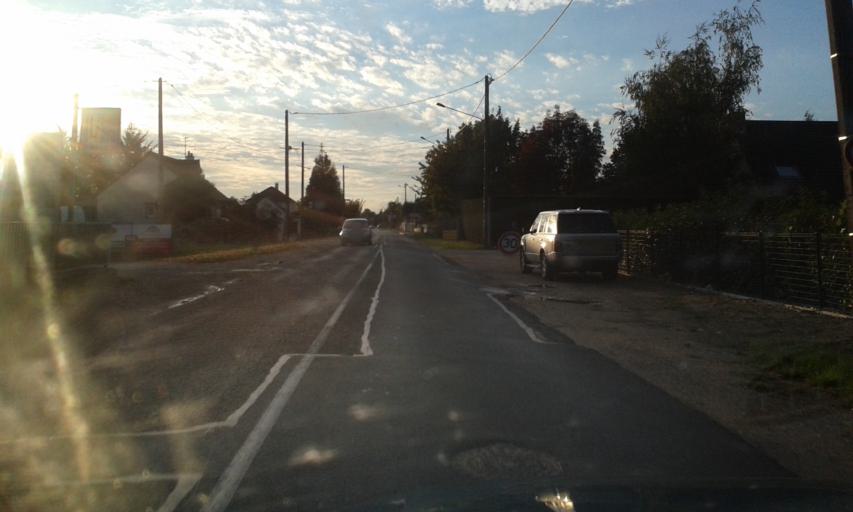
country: FR
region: Centre
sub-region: Departement du Loiret
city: Saint-Pryve-Saint-Mesmin
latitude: 47.8686
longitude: 1.8548
